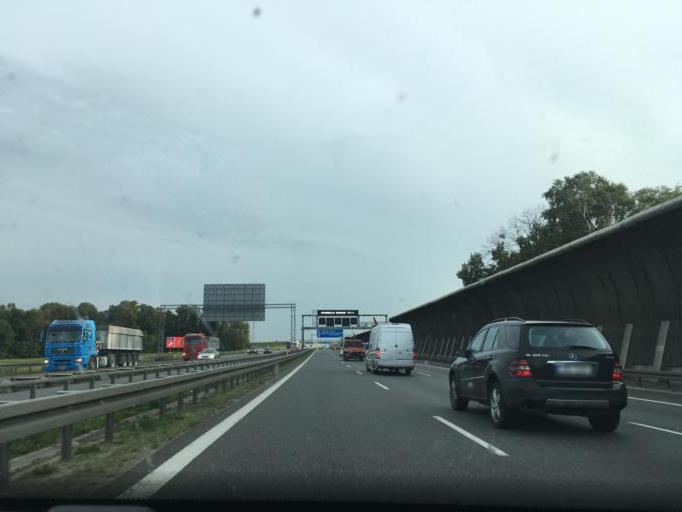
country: PL
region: Lower Silesian Voivodeship
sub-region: Powiat wroclawski
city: Tyniec Maly
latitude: 51.0607
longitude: 16.9304
